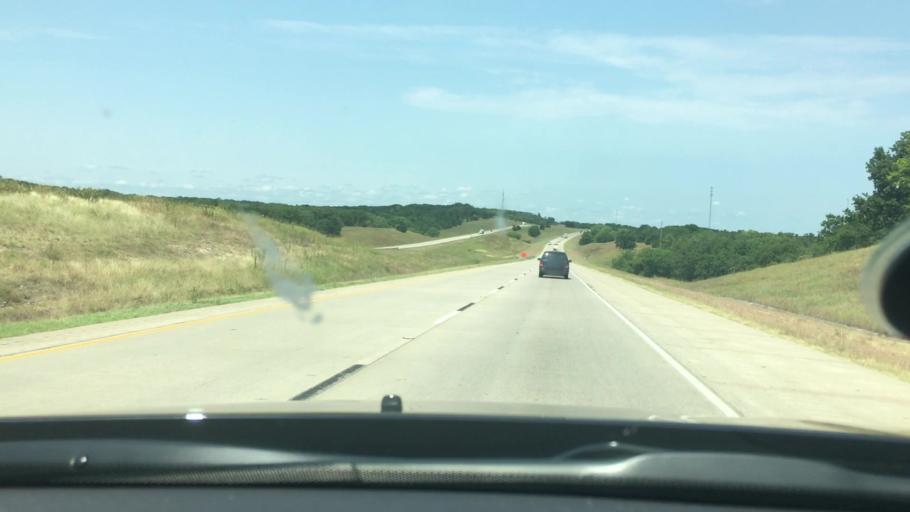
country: US
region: Oklahoma
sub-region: Love County
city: Marietta
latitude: 33.9840
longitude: -97.1359
